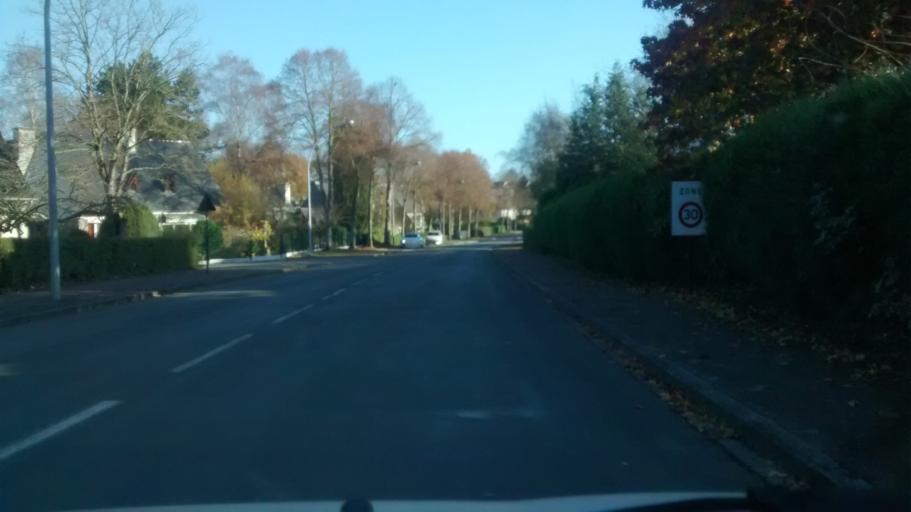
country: FR
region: Brittany
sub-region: Departement d'Ille-et-Vilaine
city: Pace
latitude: 48.1508
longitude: -1.7789
